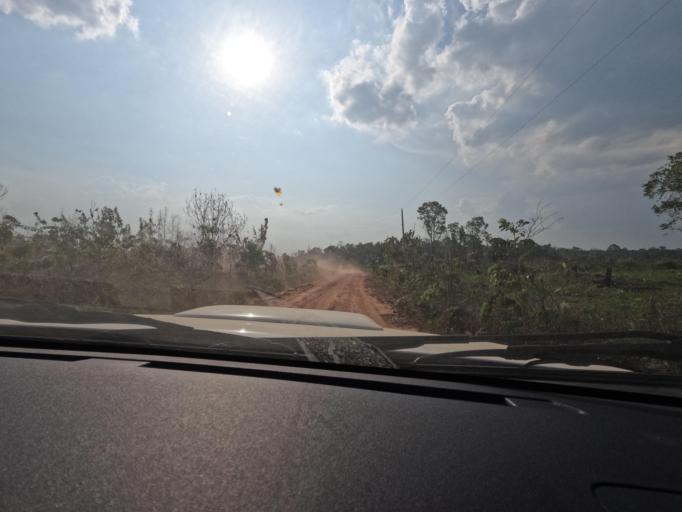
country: BR
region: Rondonia
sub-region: Porto Velho
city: Porto Velho
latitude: -8.5737
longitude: -64.0113
